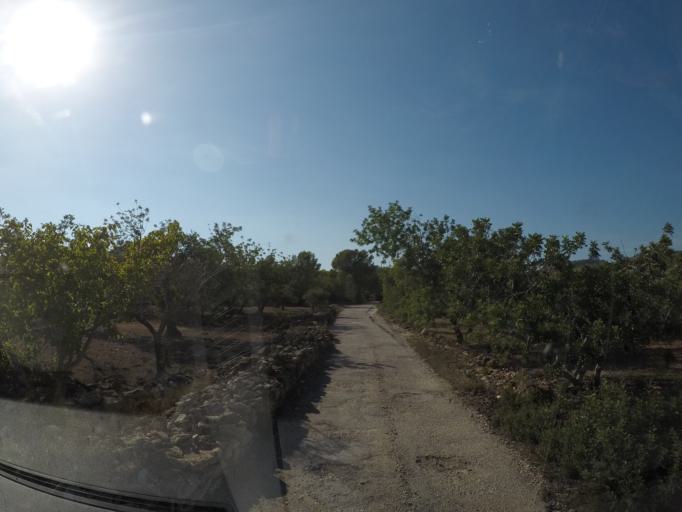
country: ES
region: Catalonia
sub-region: Provincia de Tarragona
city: El Perello
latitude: 40.9083
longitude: 0.7267
